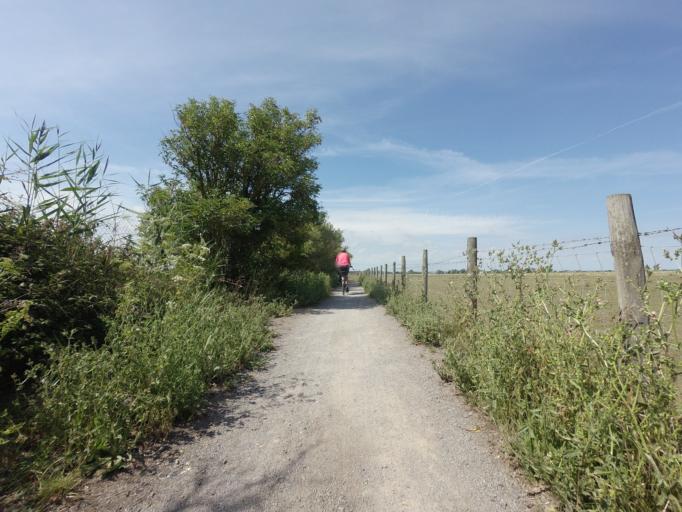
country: GB
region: England
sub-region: East Sussex
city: Rye
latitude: 50.9435
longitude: 0.7690
